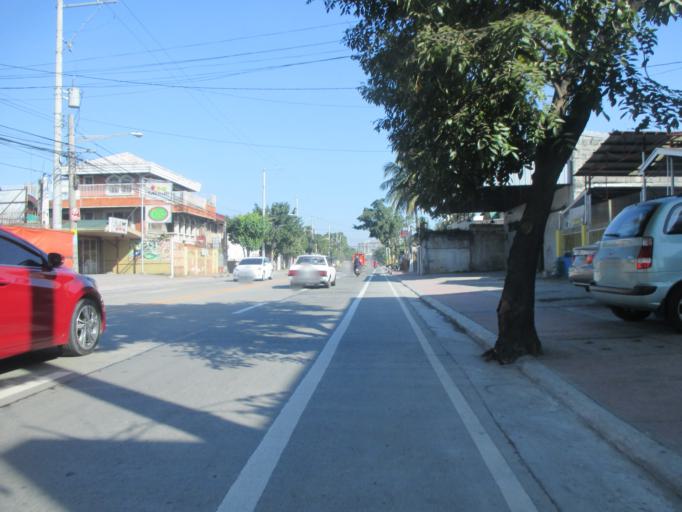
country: PH
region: Metro Manila
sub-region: Marikina
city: Calumpang
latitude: 14.6261
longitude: 121.1023
